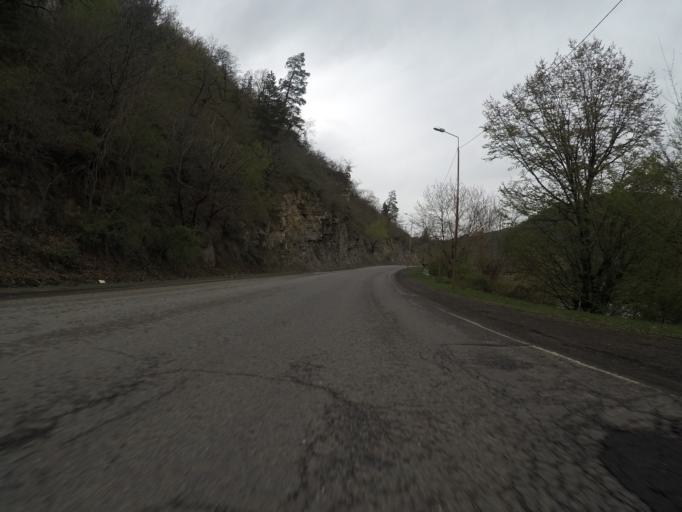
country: GE
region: Samtskhe-Javakheti
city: Borjomi
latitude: 41.8682
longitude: 43.4126
